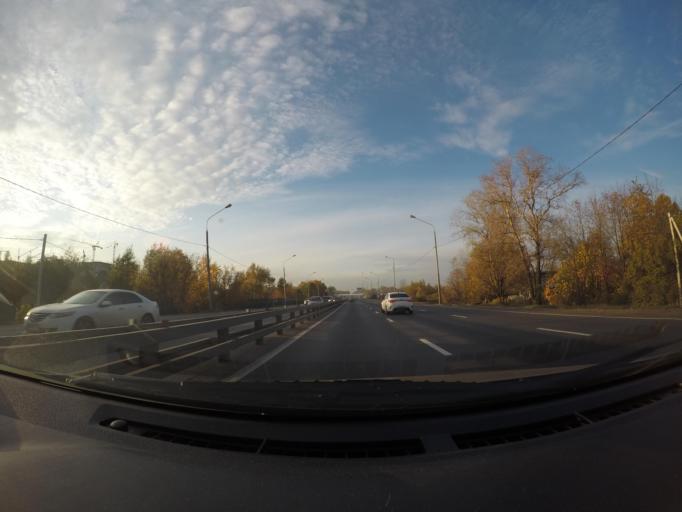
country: RU
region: Moskovskaya
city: Novopodrezkovo
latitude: 55.9369
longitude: 37.3700
